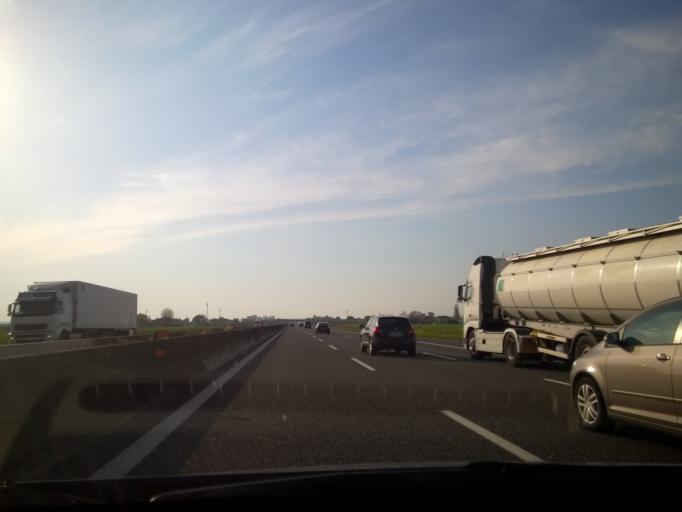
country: IT
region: Emilia-Romagna
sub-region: Provincia di Ravenna
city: Granarolo
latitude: 44.2947
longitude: 11.9777
